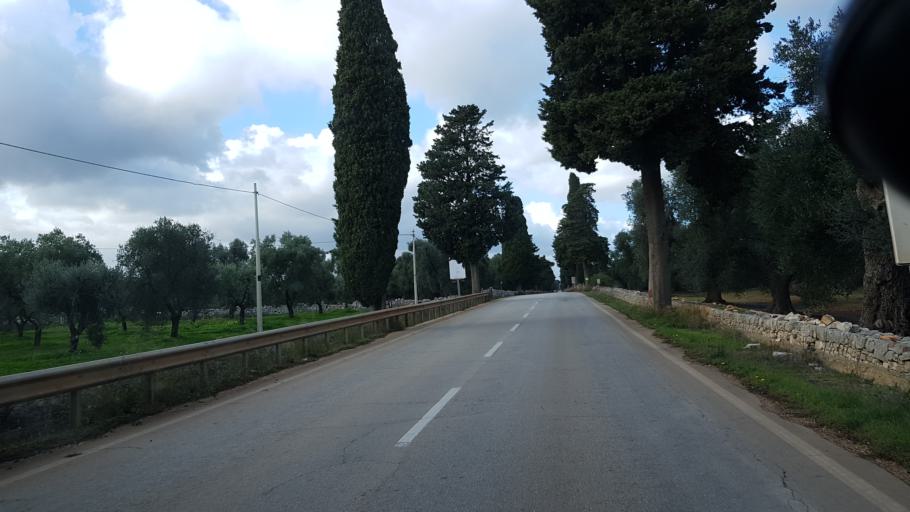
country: IT
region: Apulia
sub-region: Provincia di Brindisi
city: Montalbano
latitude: 40.7641
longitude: 17.5210
